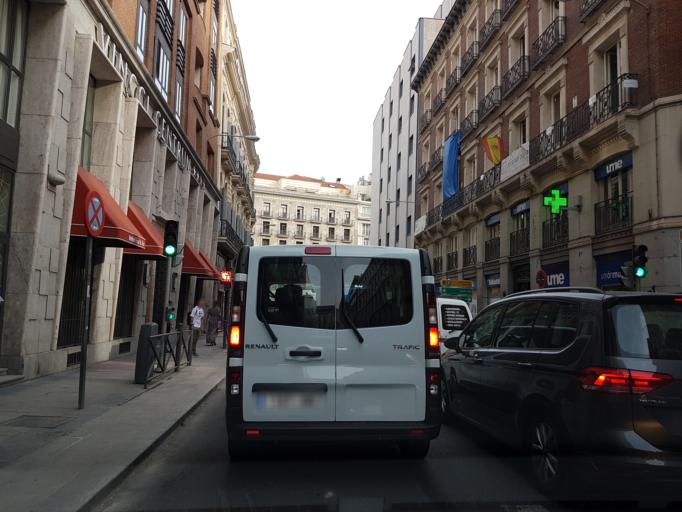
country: ES
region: Madrid
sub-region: Provincia de Madrid
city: Madrid
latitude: 40.4174
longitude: -3.6984
